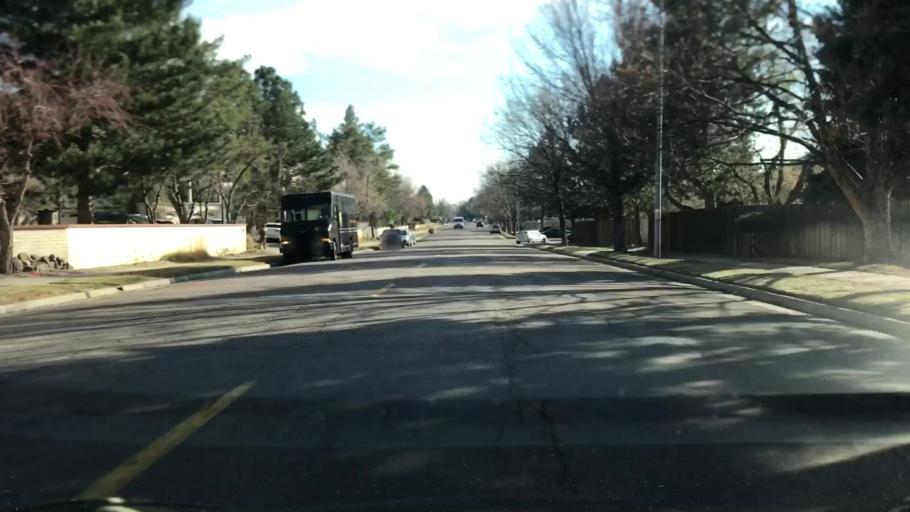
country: US
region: Colorado
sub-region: Arapahoe County
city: Glendale
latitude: 39.6882
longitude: -104.8957
